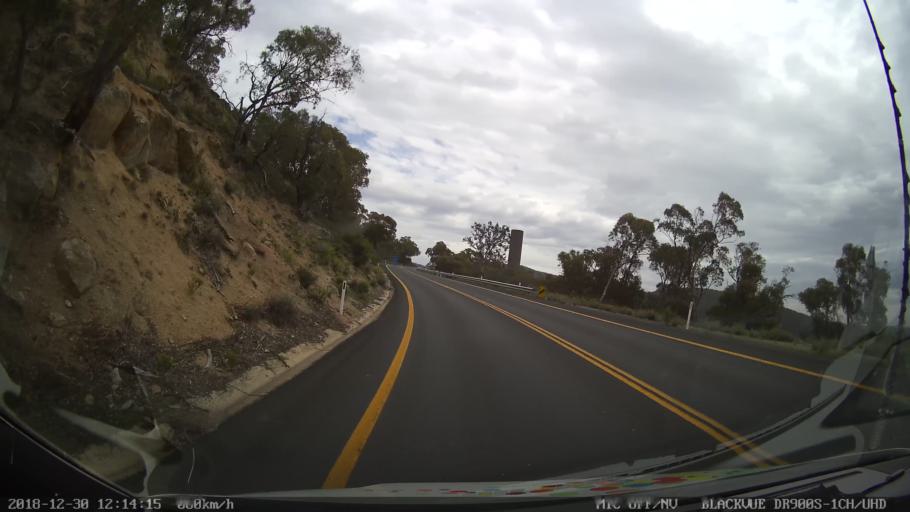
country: AU
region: New South Wales
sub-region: Snowy River
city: Jindabyne
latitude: -36.3445
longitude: 148.5814
